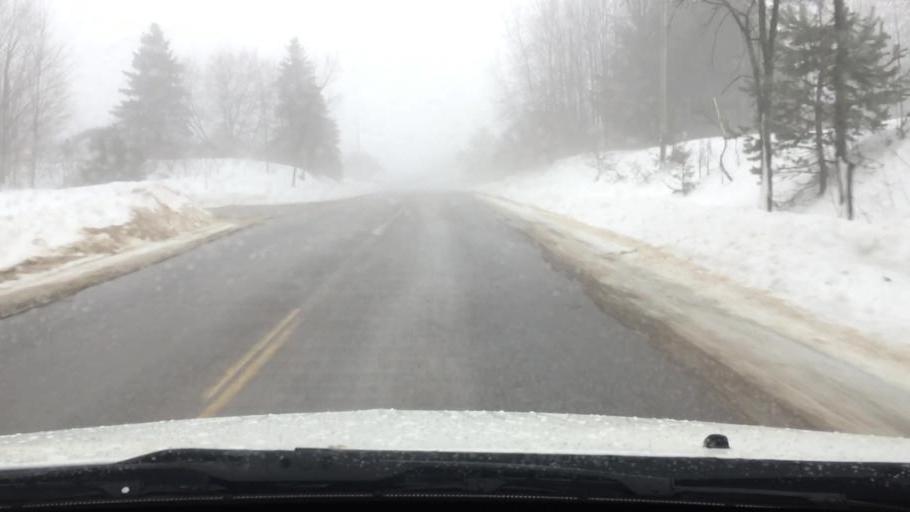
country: US
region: Michigan
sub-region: Charlevoix County
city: East Jordan
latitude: 45.1255
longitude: -85.1801
